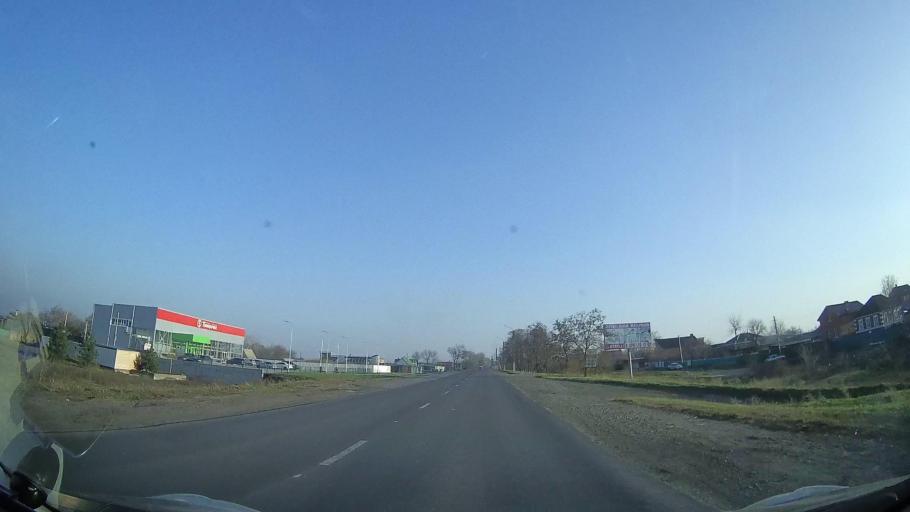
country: RU
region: Rostov
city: Ol'ginskaya
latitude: 47.2000
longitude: 39.9341
